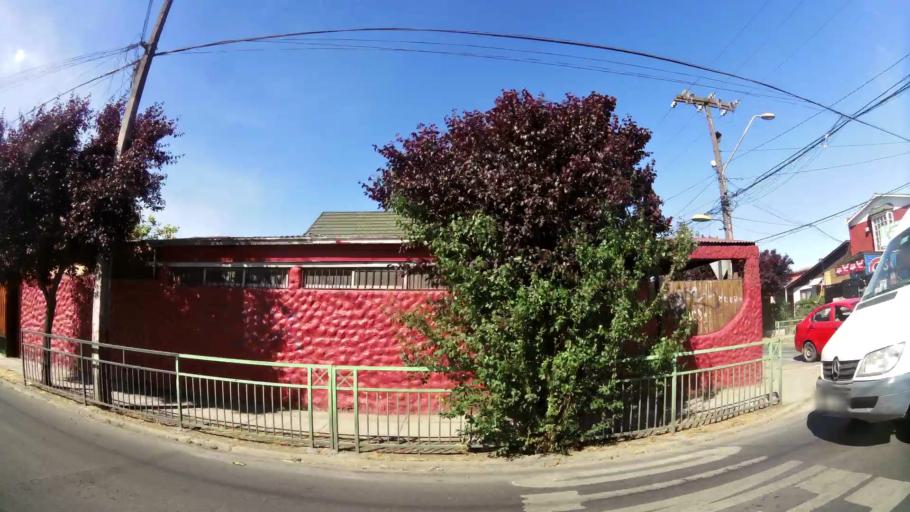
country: CL
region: Santiago Metropolitan
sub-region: Provincia de Maipo
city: San Bernardo
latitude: -33.5291
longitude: -70.7737
